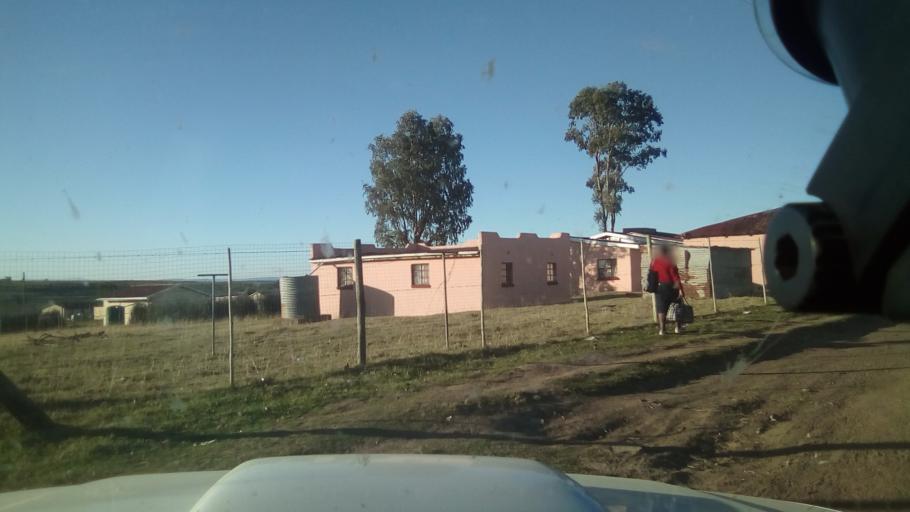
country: ZA
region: Eastern Cape
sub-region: Buffalo City Metropolitan Municipality
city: Bhisho
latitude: -32.9506
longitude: 27.2915
